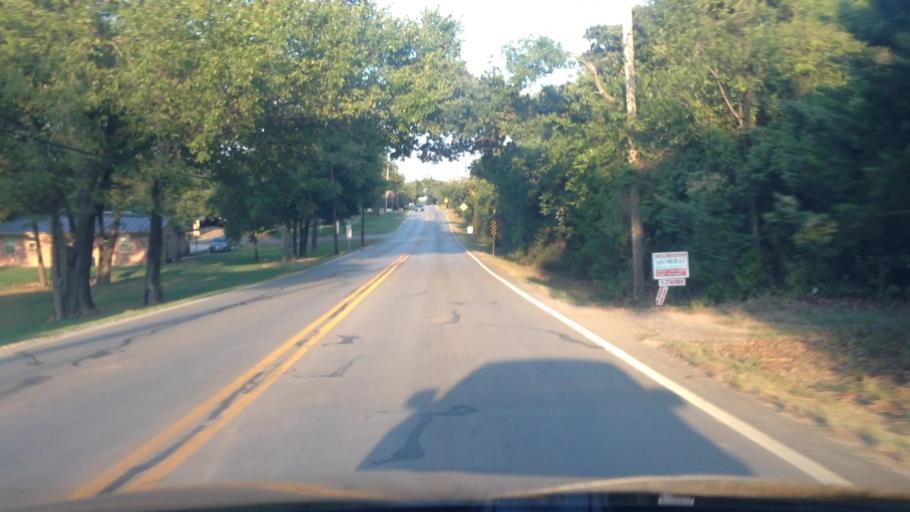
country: US
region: Texas
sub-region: Tarrant County
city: Rendon
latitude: 32.6070
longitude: -97.2187
